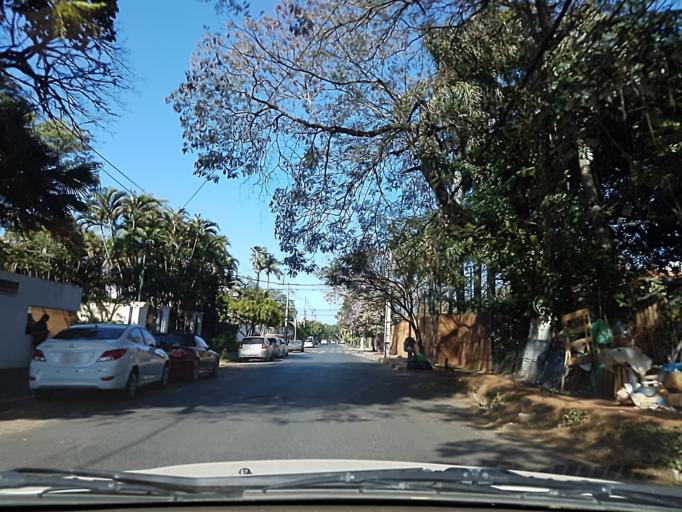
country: PY
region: Central
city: Fernando de la Mora
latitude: -25.2989
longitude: -57.5667
